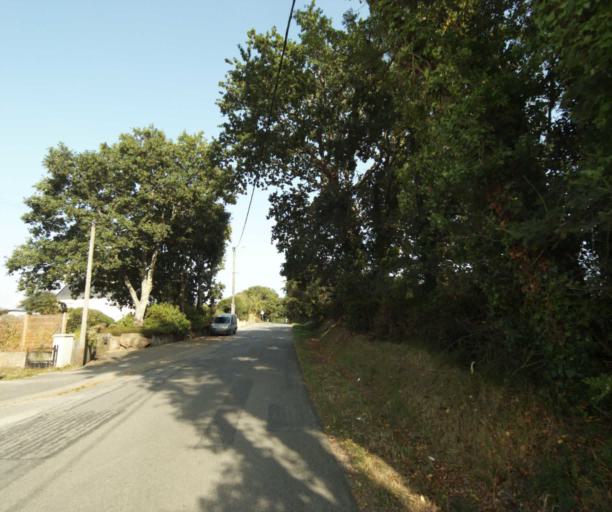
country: FR
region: Brittany
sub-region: Departement du Morbihan
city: Riantec
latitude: 47.7208
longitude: -3.3239
